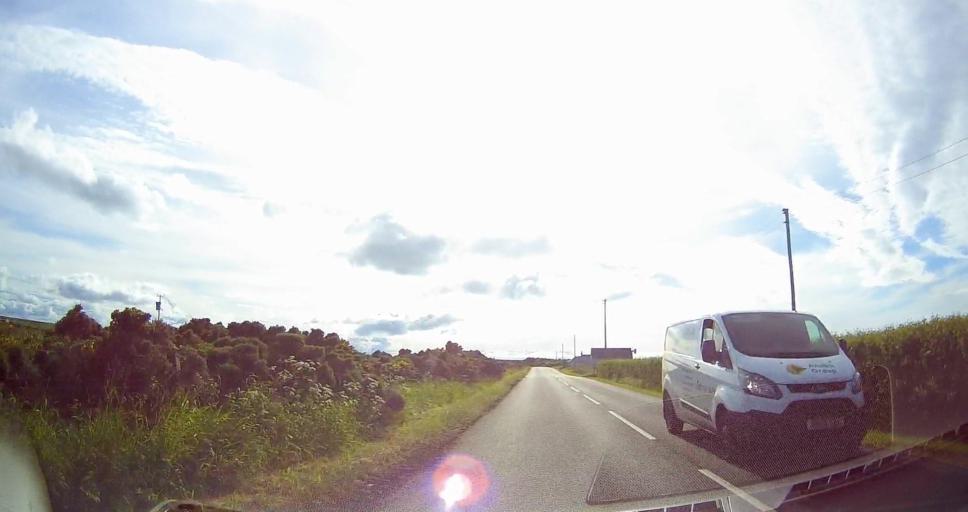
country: GB
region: Scotland
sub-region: Highland
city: Thurso
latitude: 58.6291
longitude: -3.3076
